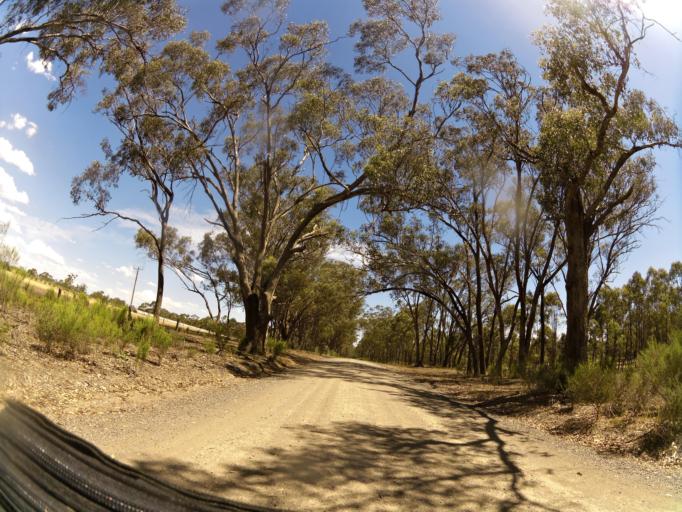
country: AU
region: Victoria
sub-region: Campaspe
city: Kyabram
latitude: -36.8187
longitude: 145.0802
